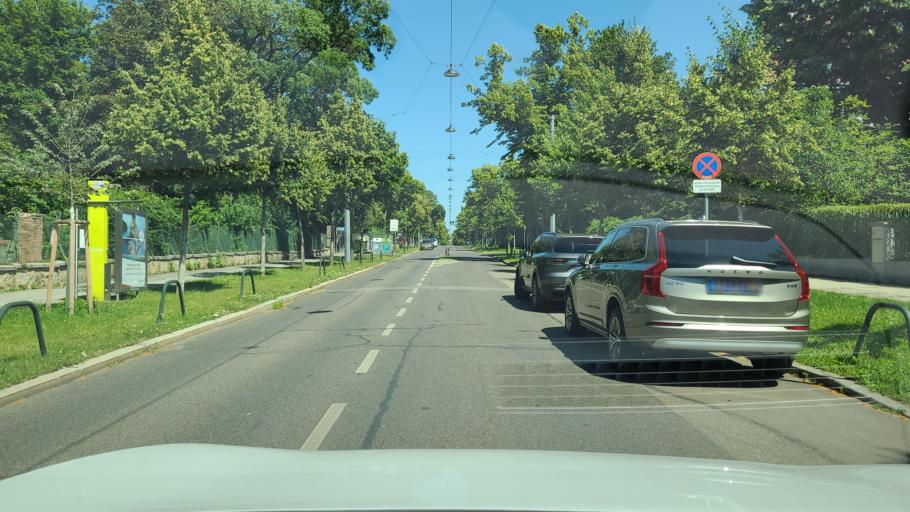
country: AT
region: Vienna
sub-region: Wien Stadt
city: Vienna
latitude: 48.2338
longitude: 16.3314
